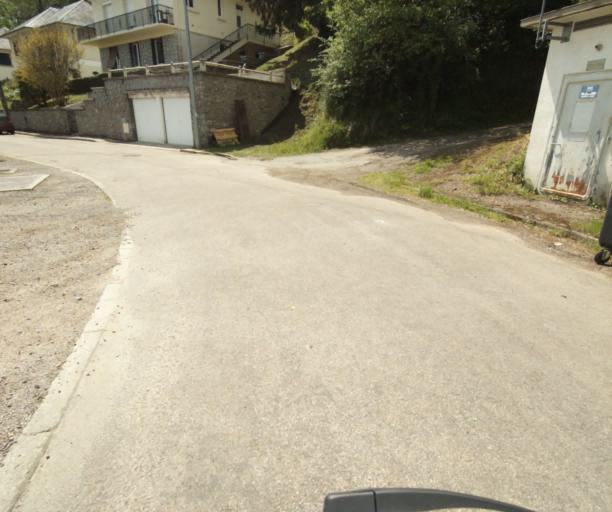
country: FR
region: Limousin
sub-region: Departement de la Correze
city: Tulle
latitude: 45.2731
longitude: 1.7646
